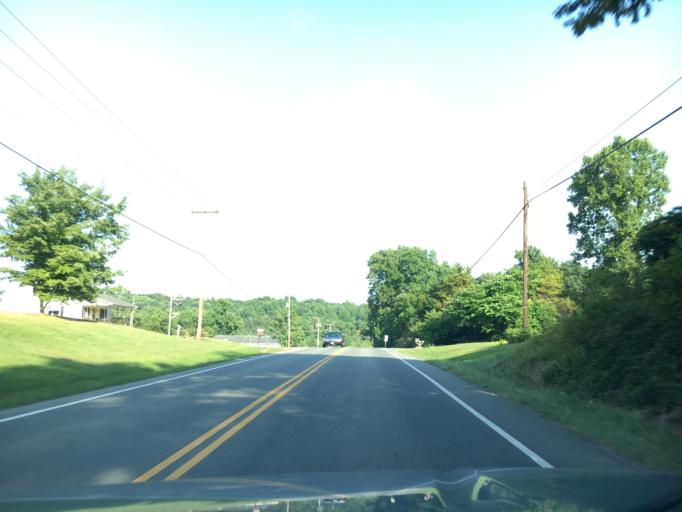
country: US
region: Virginia
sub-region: Franklin County
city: Union Hall
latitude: 37.0050
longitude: -79.7748
